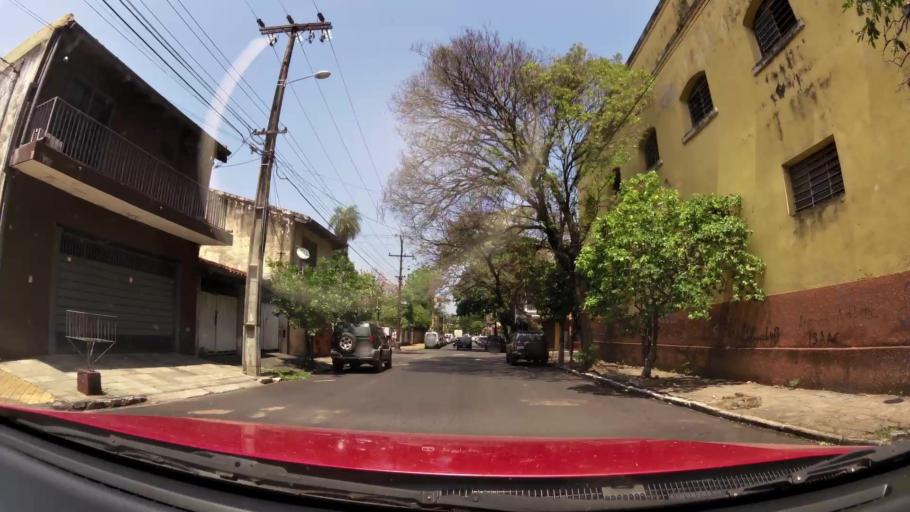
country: PY
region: Asuncion
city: Asuncion
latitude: -25.2932
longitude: -57.6418
